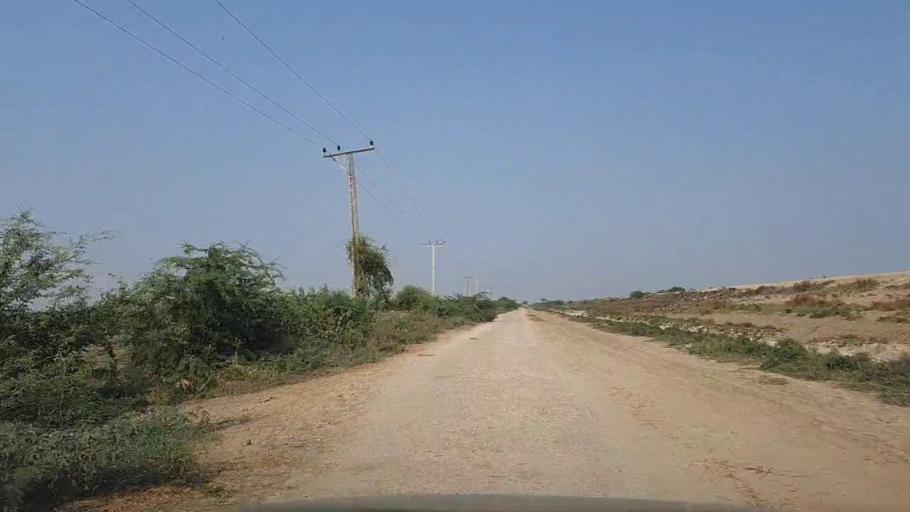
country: PK
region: Sindh
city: Chuhar Jamali
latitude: 24.5155
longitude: 67.9251
